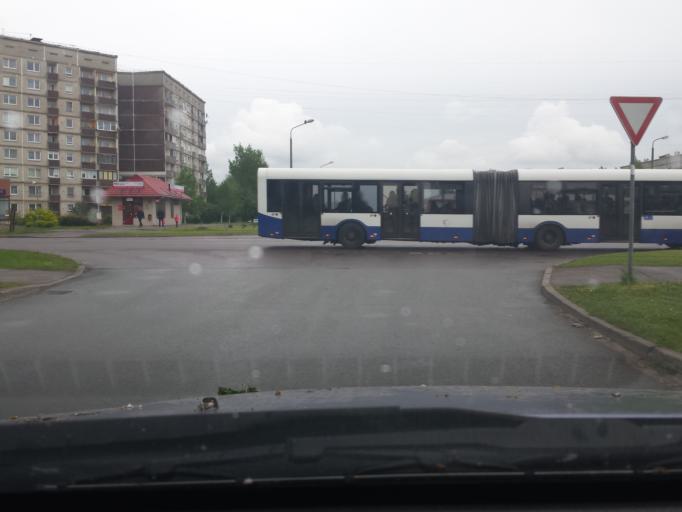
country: LV
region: Riga
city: Riga
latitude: 56.9484
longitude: 24.1962
